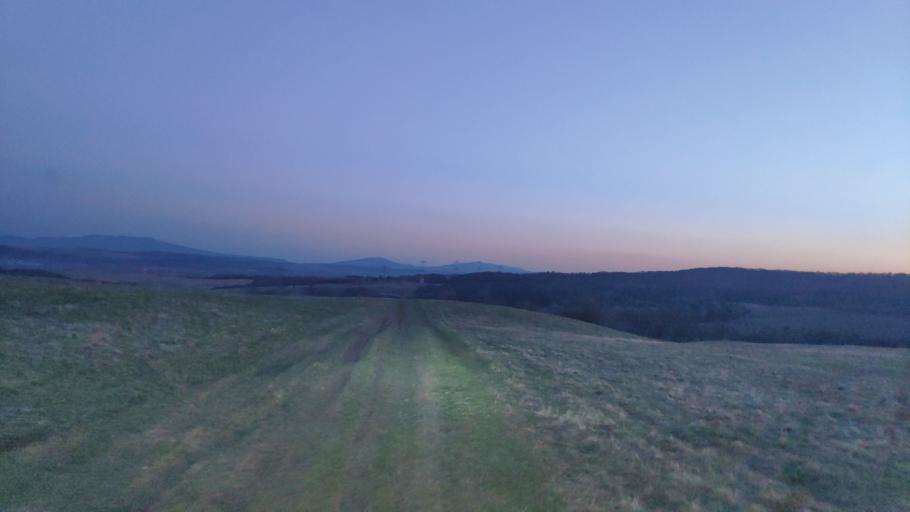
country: SK
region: Kosicky
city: Kosice
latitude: 48.8282
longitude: 21.2624
